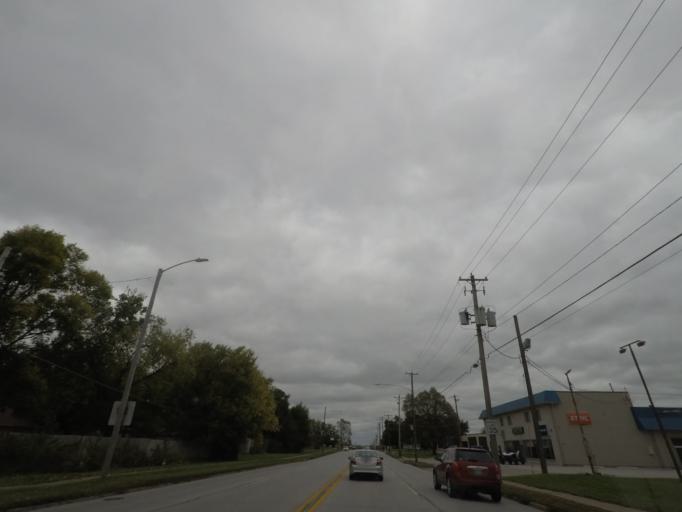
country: US
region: Iowa
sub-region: Polk County
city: Ankeny
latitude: 41.7257
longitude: -93.6004
